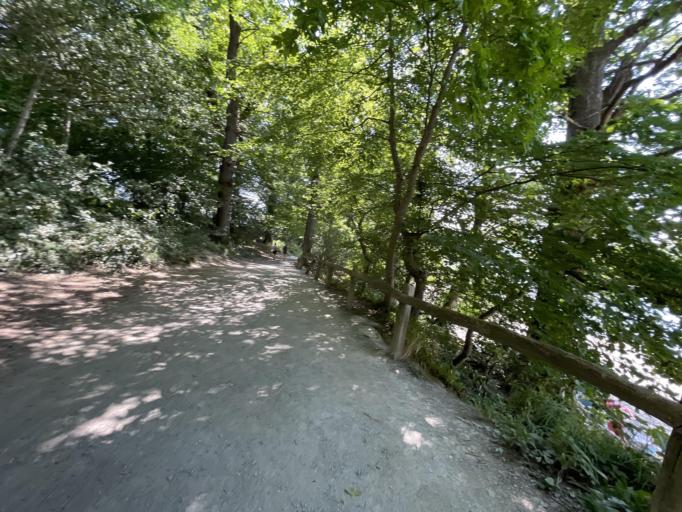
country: GB
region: England
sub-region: Cumbria
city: Keswick
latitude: 54.5921
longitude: -3.1406
